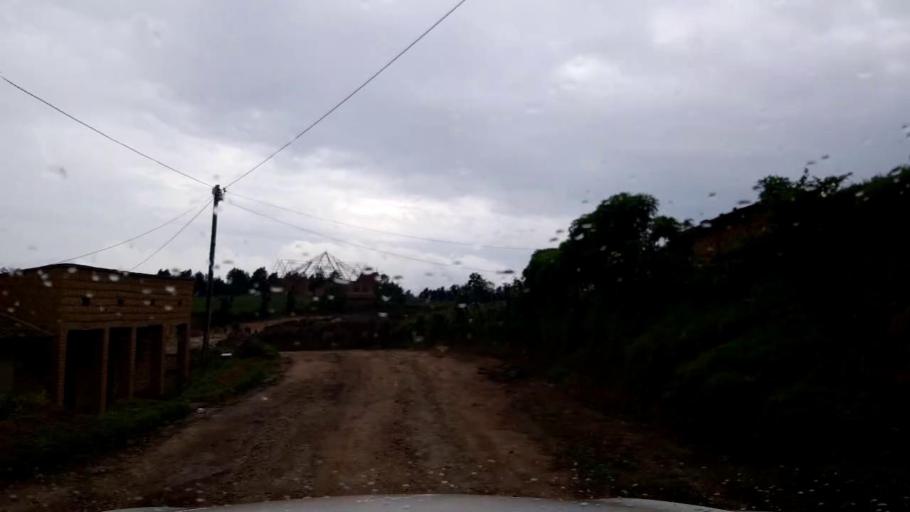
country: RW
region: Western Province
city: Kibuye
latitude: -2.0136
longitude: 29.4713
